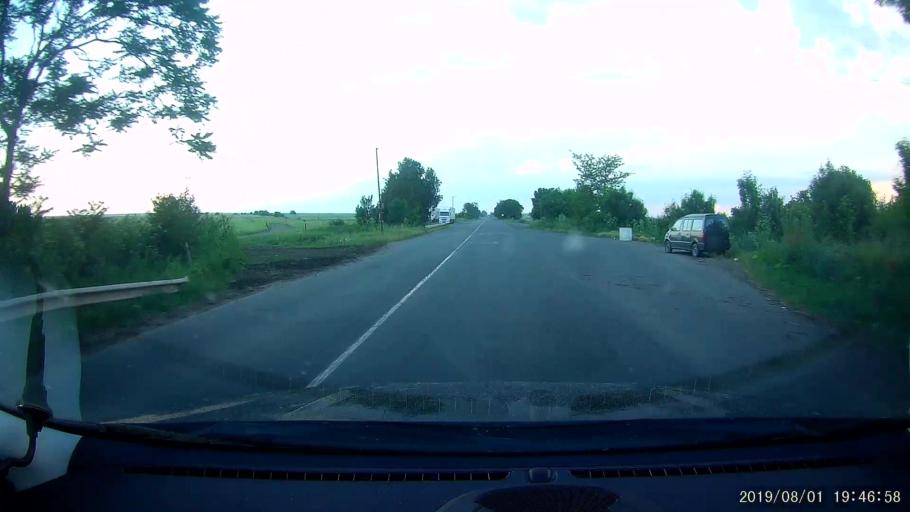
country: BG
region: Burgas
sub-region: Obshtina Karnobat
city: Karnobat
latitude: 42.6503
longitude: 26.9647
